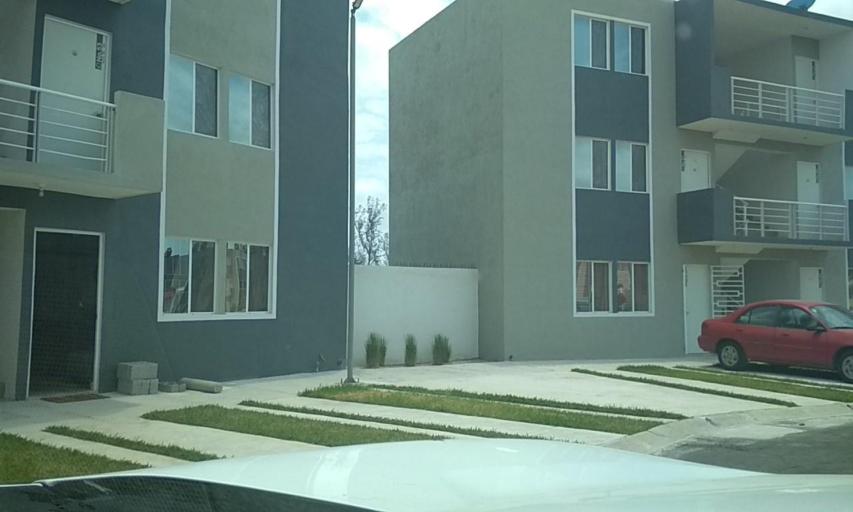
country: MX
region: Veracruz
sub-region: Veracruz
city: Las Amapolas
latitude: 19.1472
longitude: -96.2153
